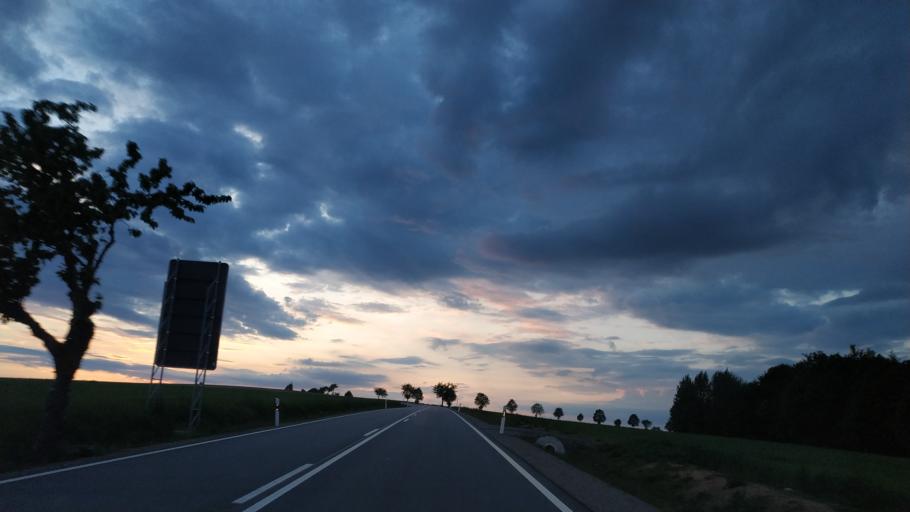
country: DE
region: Saxony
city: Hohnstein
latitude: 50.9866
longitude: 14.0888
